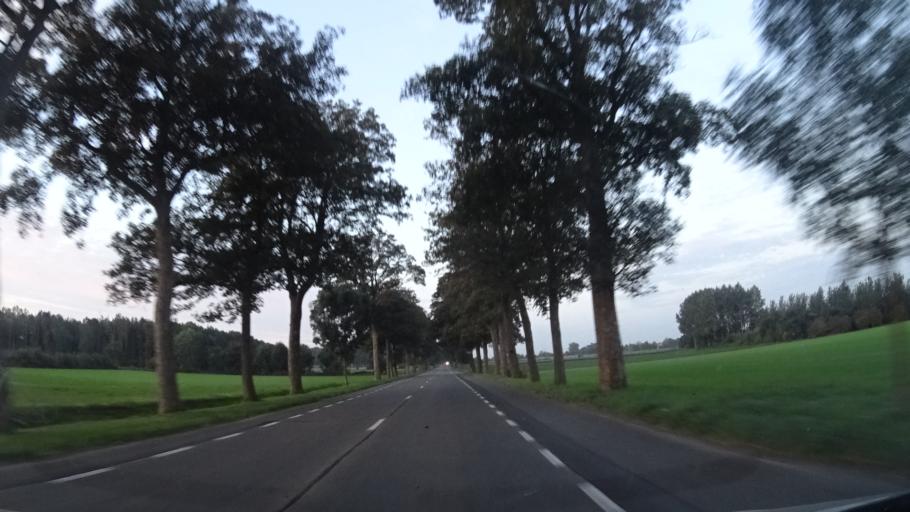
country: BE
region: Wallonia
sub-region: Province du Hainaut
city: Peruwelz
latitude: 50.5573
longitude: 3.6097
